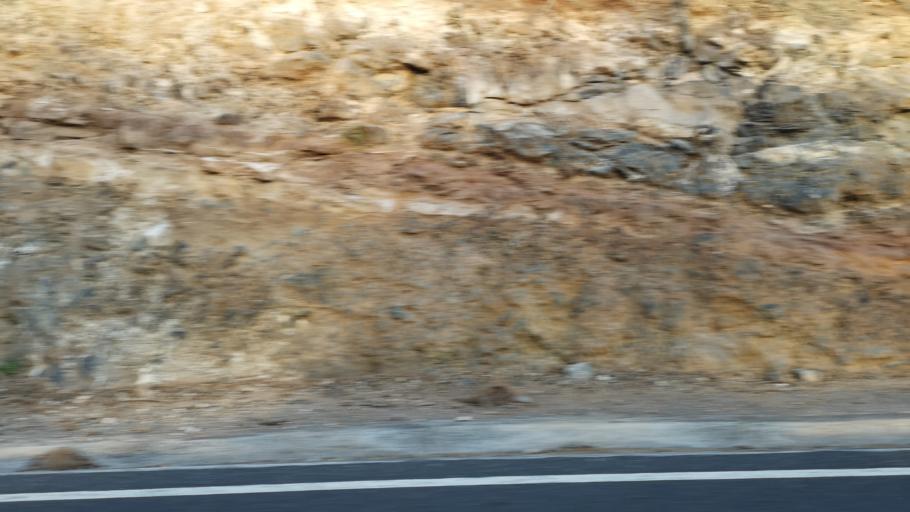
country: ES
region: Canary Islands
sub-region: Provincia de Santa Cruz de Tenerife
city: Alajero
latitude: 28.0331
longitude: -17.1923
